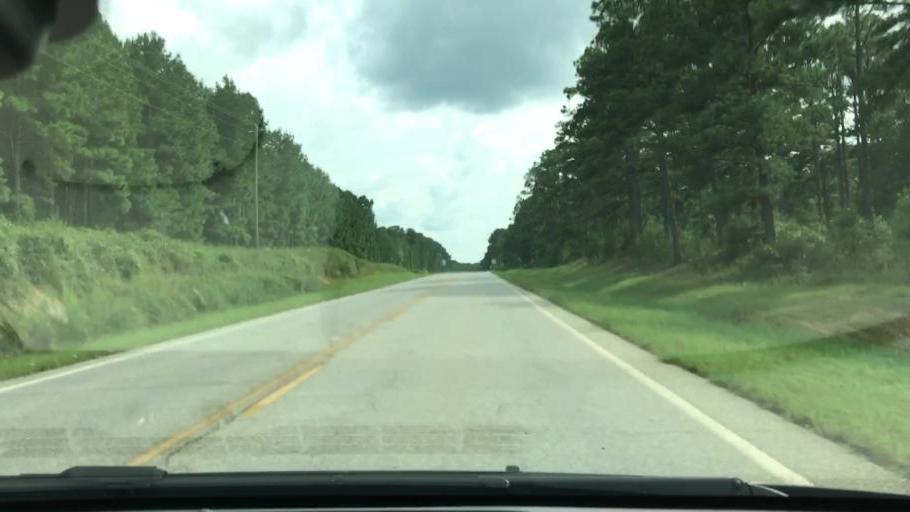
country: US
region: Georgia
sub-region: Clay County
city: Fort Gaines
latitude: 31.6432
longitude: -85.0440
